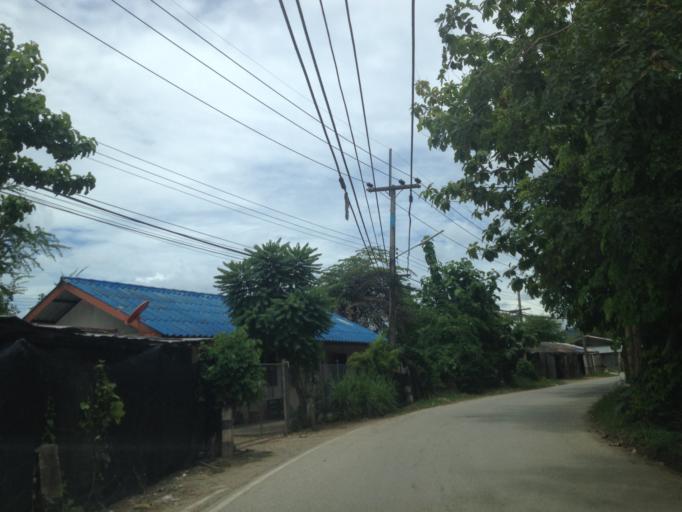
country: TH
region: Chiang Mai
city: Hang Dong
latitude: 18.7197
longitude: 98.9334
